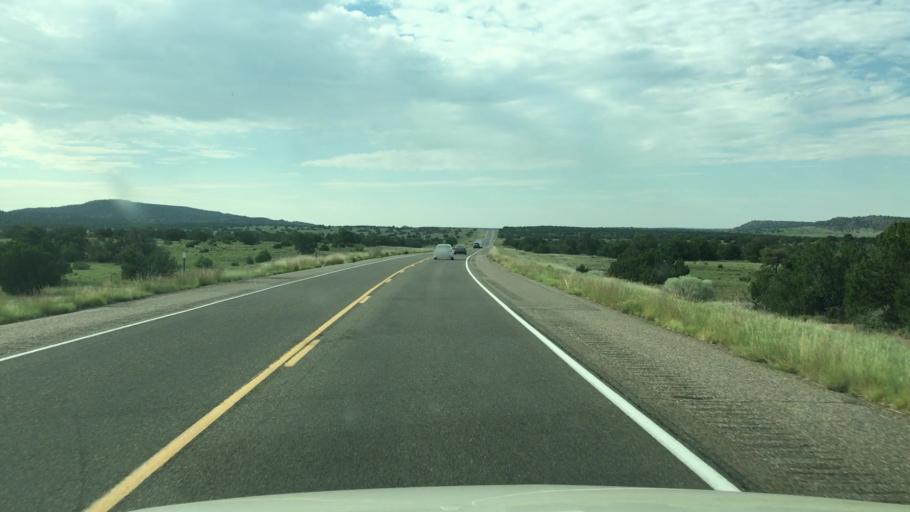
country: US
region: New Mexico
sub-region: Santa Fe County
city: Eldorado at Santa Fe
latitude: 35.3284
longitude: -105.8337
